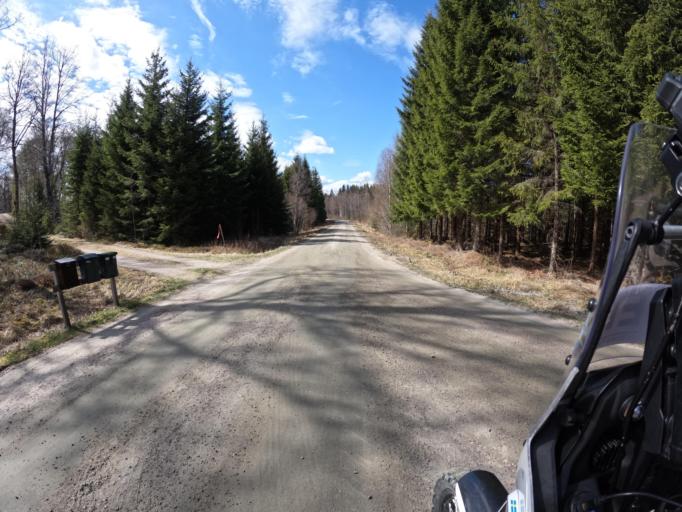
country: SE
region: Vaestra Goetaland
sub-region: Ulricehamns Kommun
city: Ulricehamn
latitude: 57.9283
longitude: 13.5595
